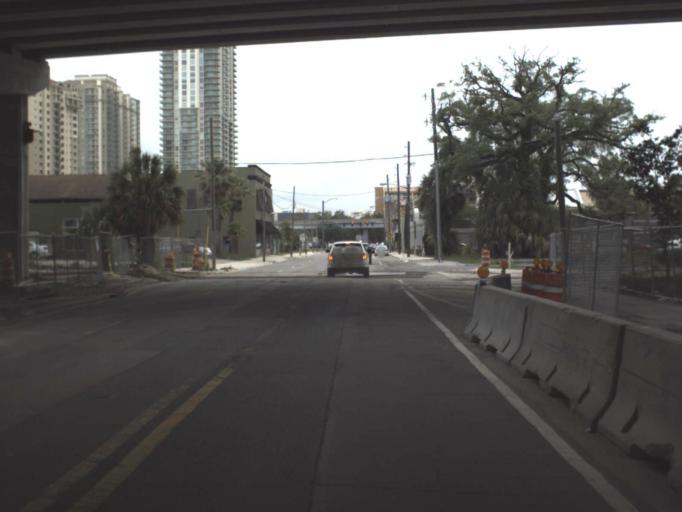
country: US
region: Florida
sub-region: Duval County
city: Jacksonville
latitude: 30.3141
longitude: -81.6538
